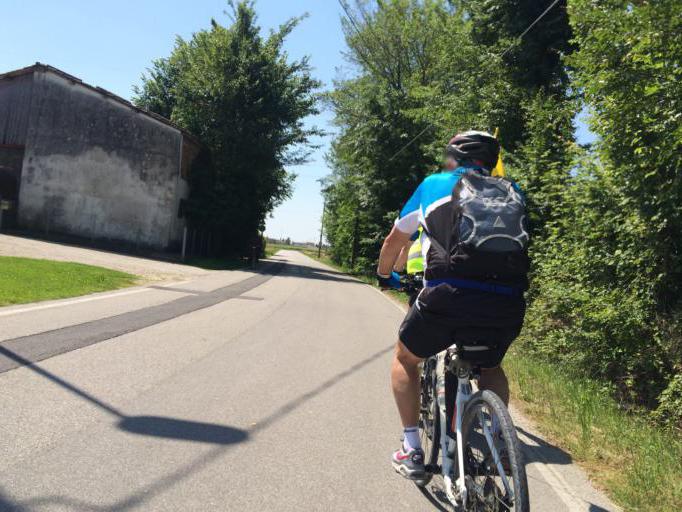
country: IT
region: Veneto
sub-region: Provincia di Vicenza
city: Ponte di Castegnero
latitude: 45.4304
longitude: 11.6093
